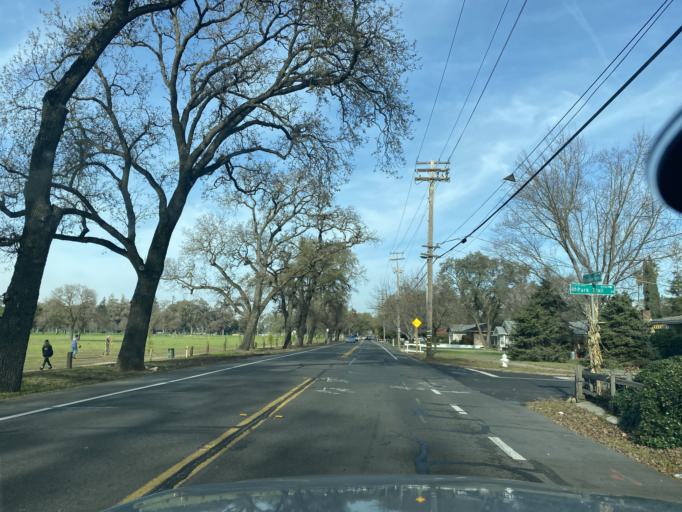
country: US
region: California
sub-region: Sacramento County
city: Elk Grove
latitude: 38.3920
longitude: -121.3714
